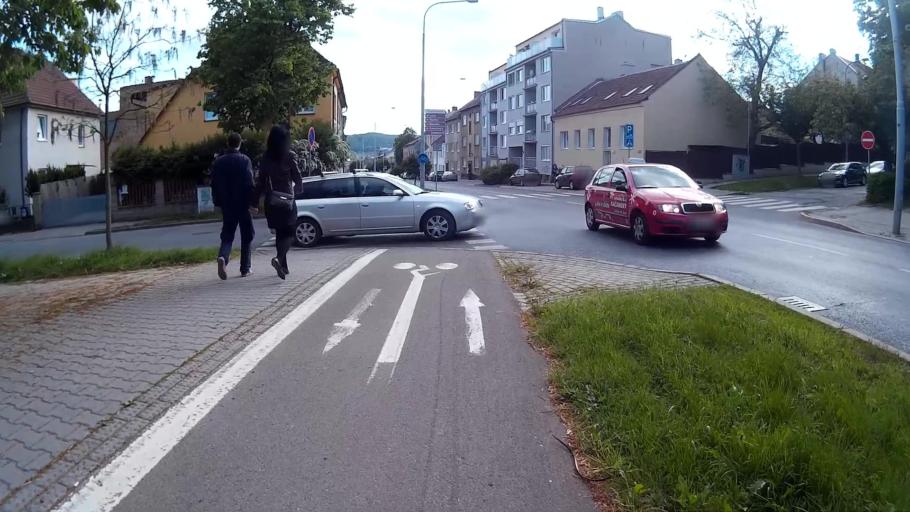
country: CZ
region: South Moravian
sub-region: Mesto Brno
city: Brno
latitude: 49.2170
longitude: 16.5718
